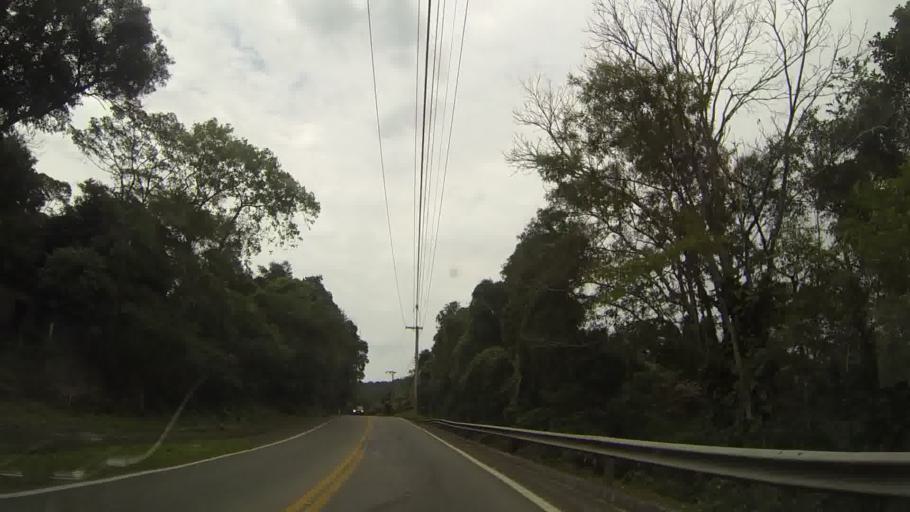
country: BR
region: Sao Paulo
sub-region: Sao Sebastiao
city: Sao Sebastiao
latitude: -23.8312
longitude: -45.5016
